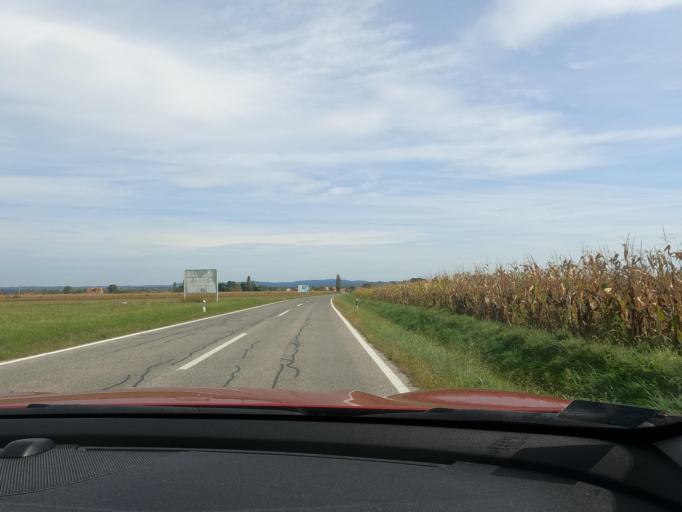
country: HR
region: Sisacko-Moslavacka
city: Osekovo
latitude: 45.5453
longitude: 16.5814
